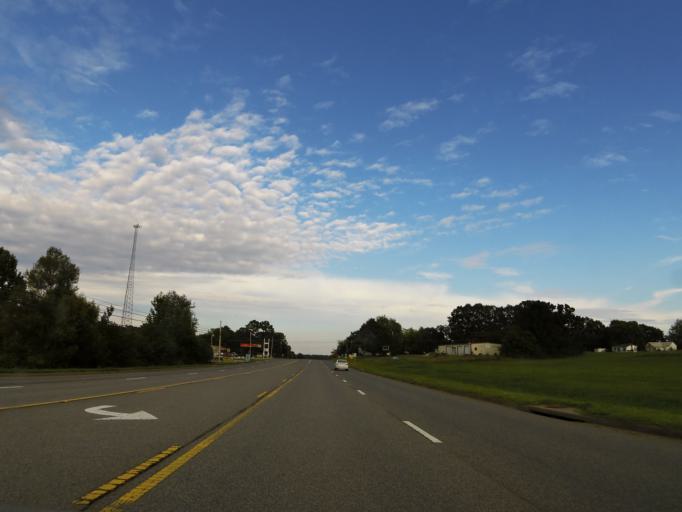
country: US
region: Alabama
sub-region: Lauderdale County
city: Rogersville
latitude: 34.8133
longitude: -87.2527
